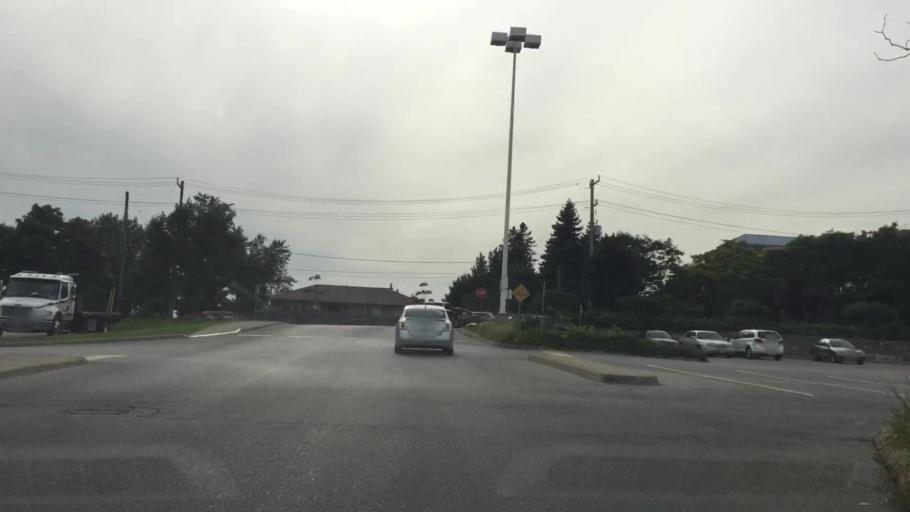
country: CA
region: Ontario
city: Scarborough
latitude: 43.7574
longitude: -79.2318
